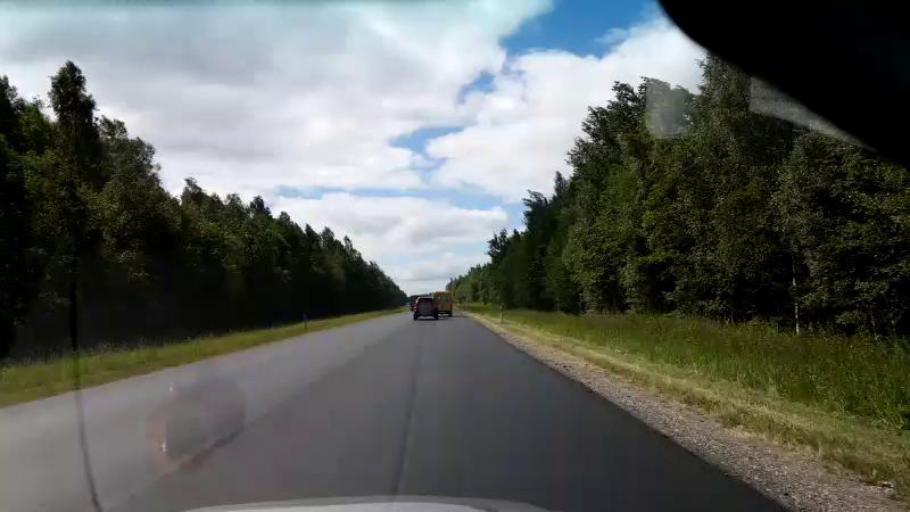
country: LV
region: Salacgrivas
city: Ainazi
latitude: 57.9727
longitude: 24.4523
